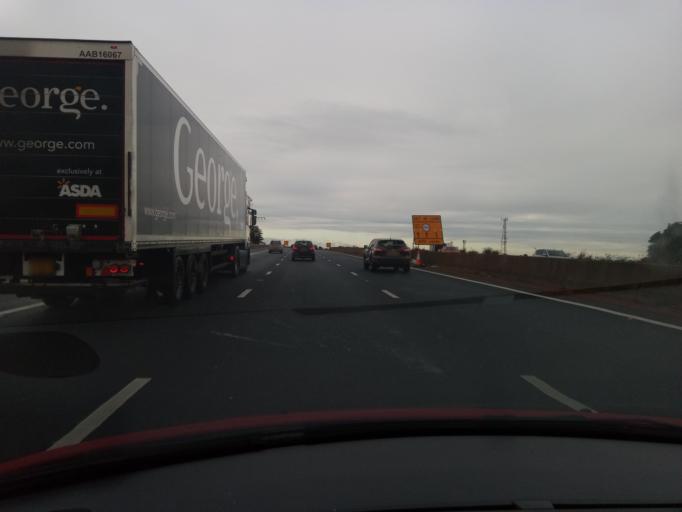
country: GB
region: England
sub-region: North Yorkshire
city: Ripon
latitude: 54.2223
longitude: -1.4860
